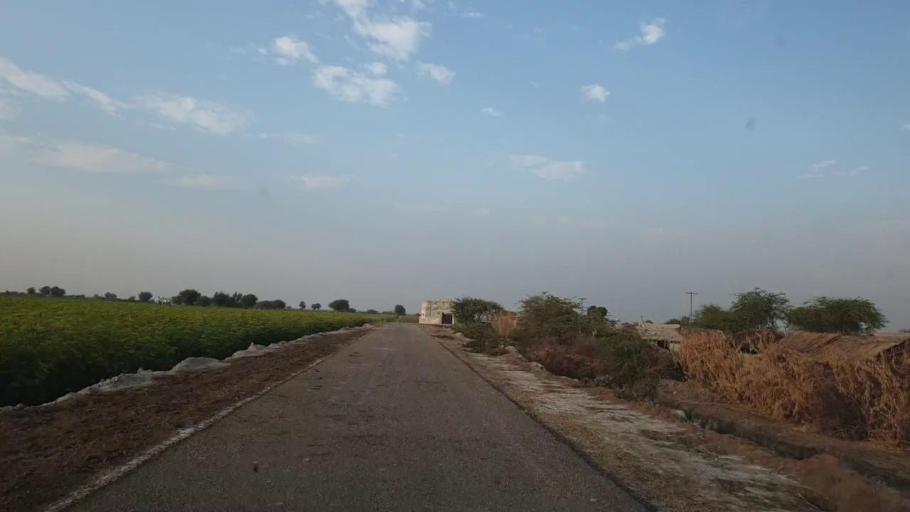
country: PK
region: Sindh
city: Pithoro
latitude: 25.5951
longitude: 69.3117
